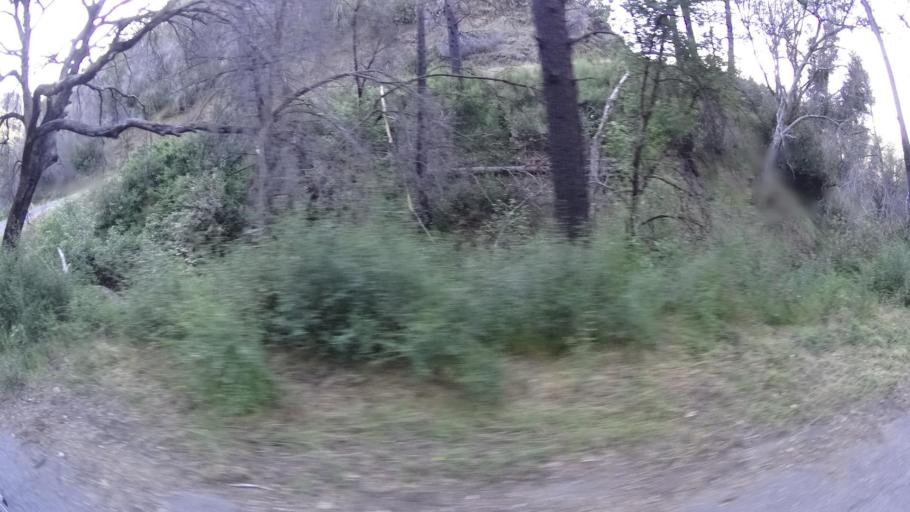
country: US
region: California
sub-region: Lake County
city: Upper Lake
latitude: 39.2600
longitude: -122.9472
